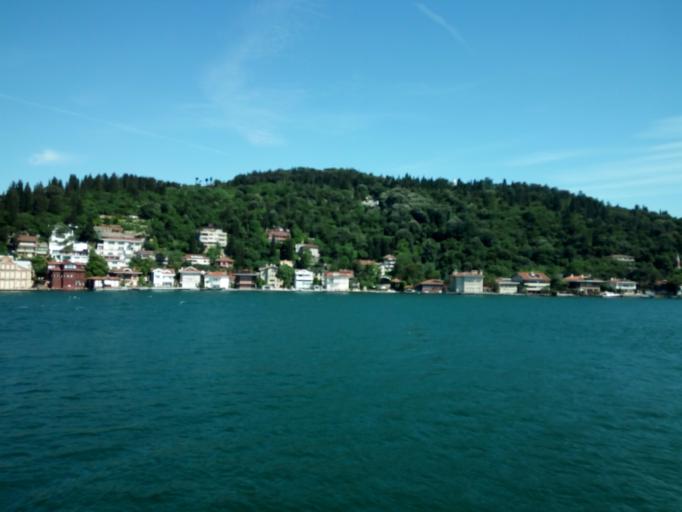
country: TR
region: Istanbul
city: UEskuedar
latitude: 41.0678
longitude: 29.0537
